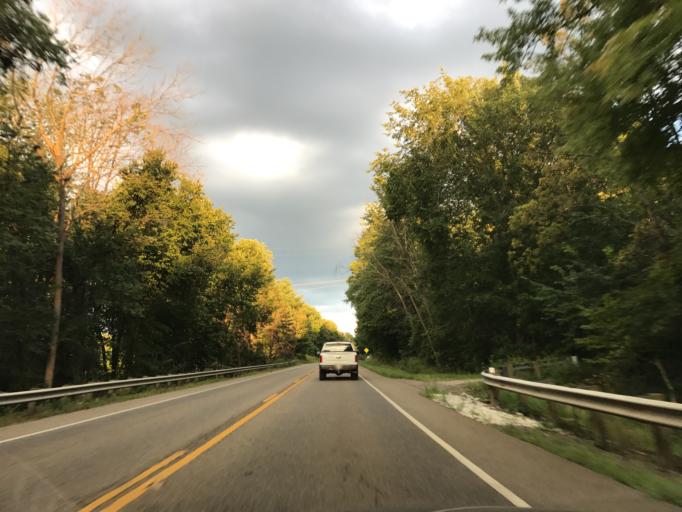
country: US
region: Ohio
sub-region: Stark County
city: East Canton
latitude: 40.7700
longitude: -81.2209
